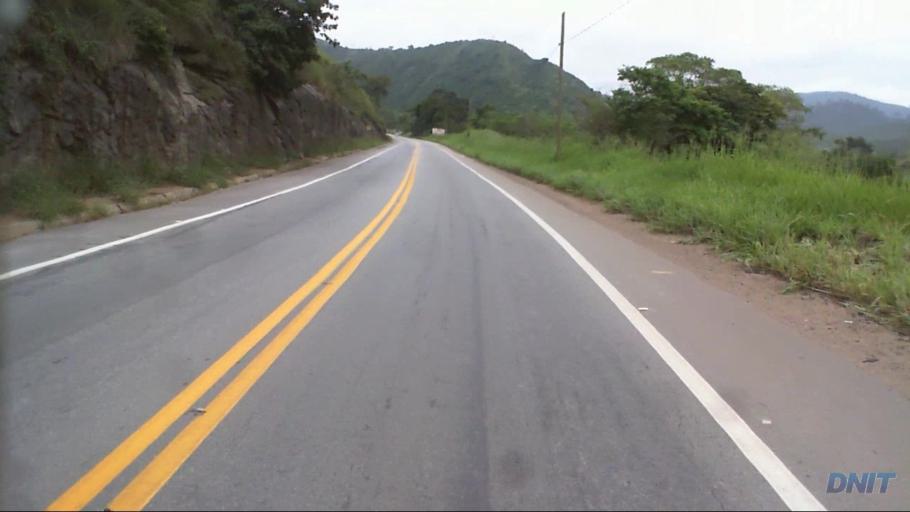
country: BR
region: Minas Gerais
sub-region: Timoteo
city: Timoteo
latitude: -19.5427
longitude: -42.6895
